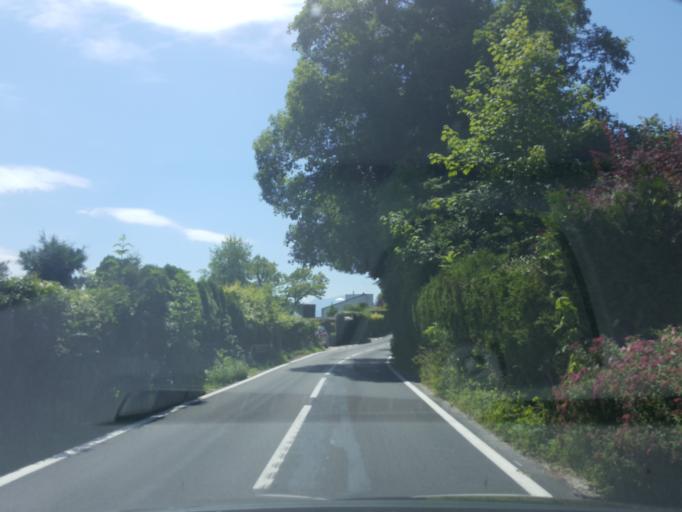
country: AT
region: Upper Austria
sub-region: Politischer Bezirk Vocklabruck
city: Seewalchen
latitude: 47.9445
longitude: 13.5719
